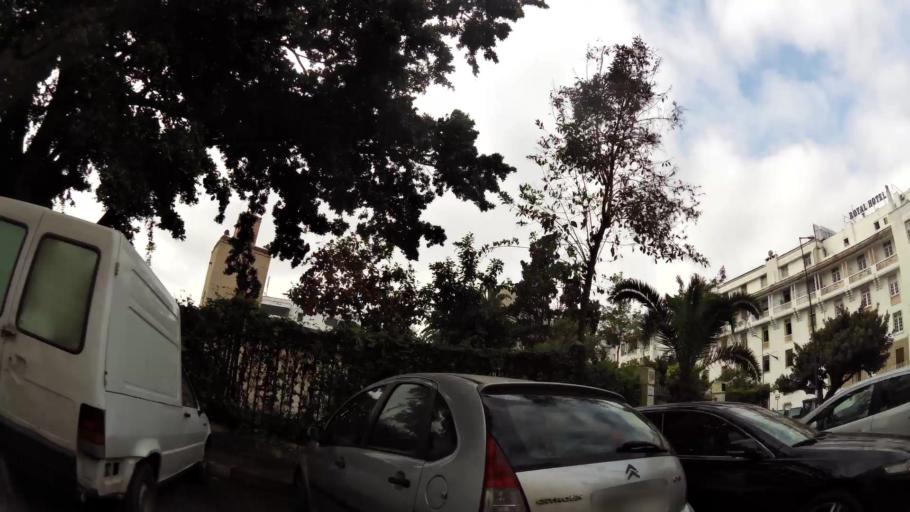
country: MA
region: Rabat-Sale-Zemmour-Zaer
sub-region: Rabat
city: Rabat
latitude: 34.0210
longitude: -6.8350
